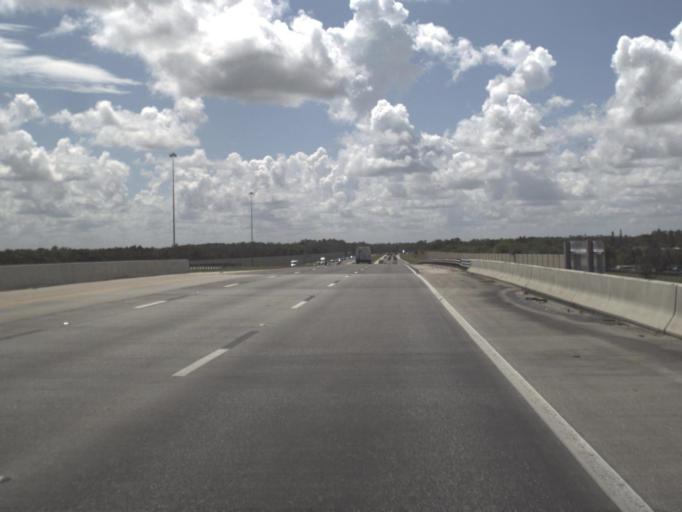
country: US
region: Florida
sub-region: Lee County
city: Estero
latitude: 26.4325
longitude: -81.7781
